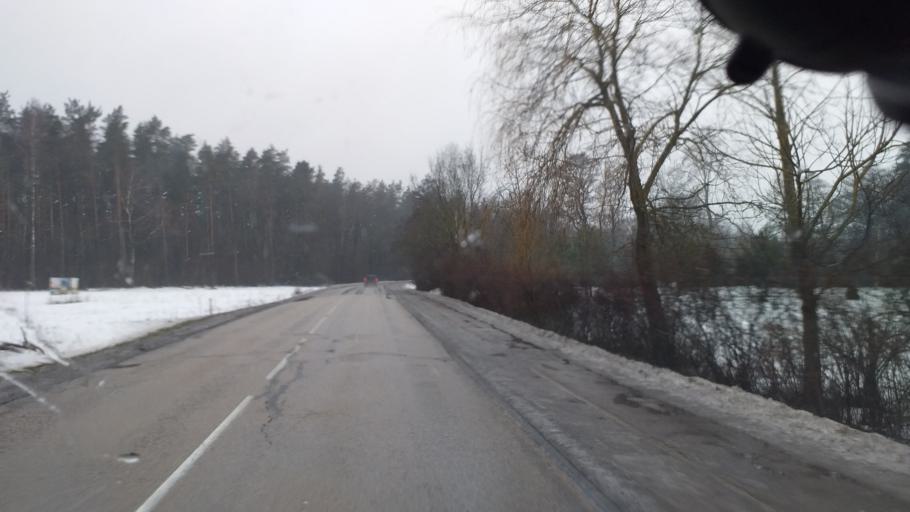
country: LV
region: Riga
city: Daugavgriva
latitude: 56.9838
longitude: 23.9997
